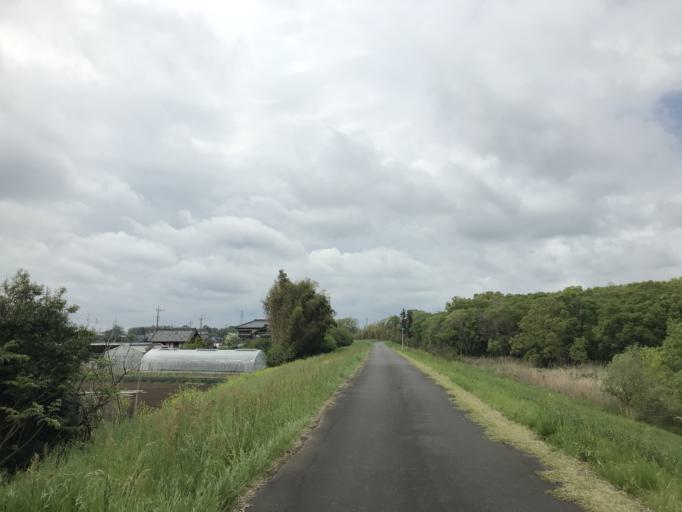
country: JP
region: Ibaraki
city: Moriya
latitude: 35.9728
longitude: 140.0021
